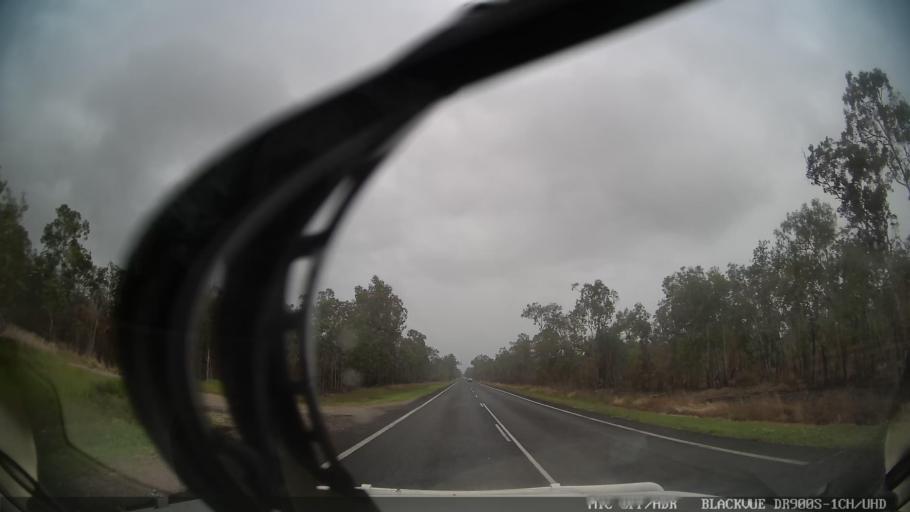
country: AU
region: Queensland
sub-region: Hinchinbrook
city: Ingham
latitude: -18.4368
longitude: 146.1392
